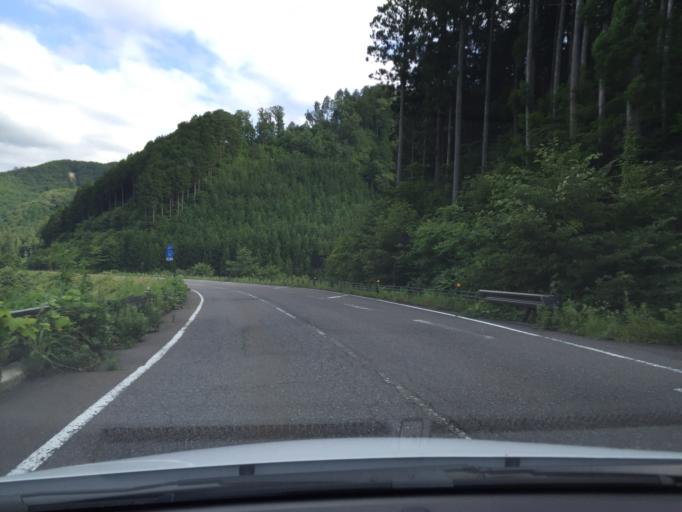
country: JP
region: Tochigi
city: Kuroiso
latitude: 37.2083
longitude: 140.0974
